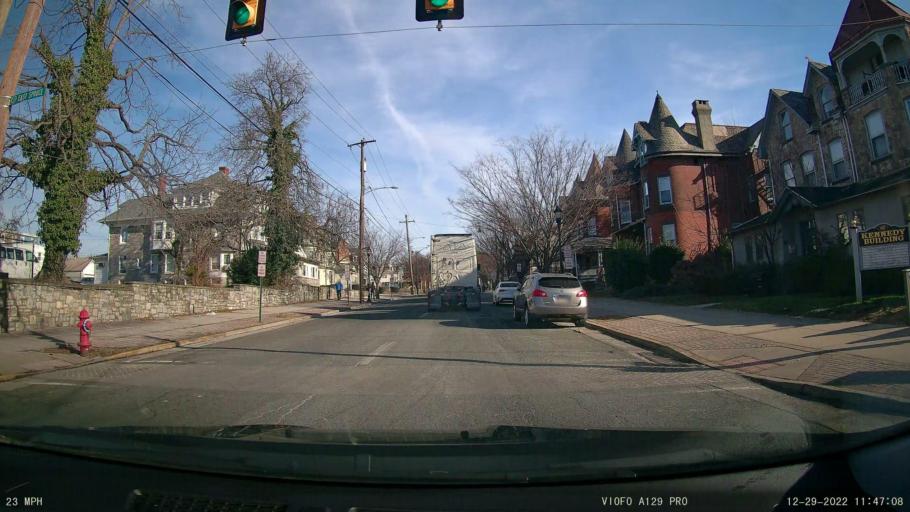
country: US
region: Pennsylvania
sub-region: Montgomery County
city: Norristown
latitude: 40.1210
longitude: -75.3367
